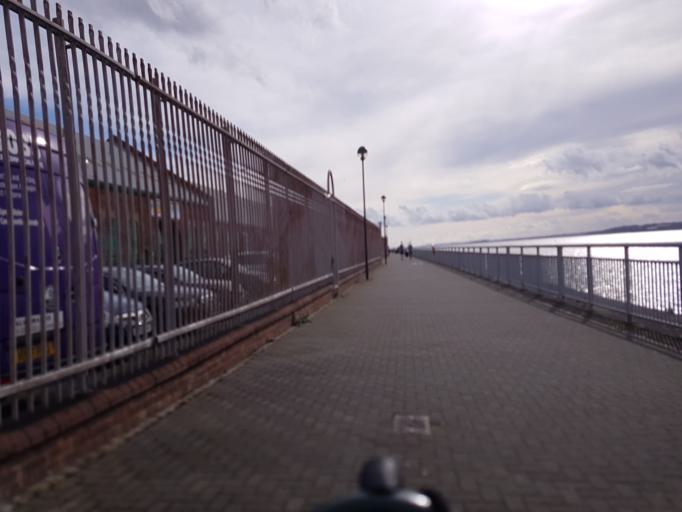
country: GB
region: England
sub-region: Metropolitan Borough of Wirral
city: New Ferry
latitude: 53.3839
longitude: -2.9817
